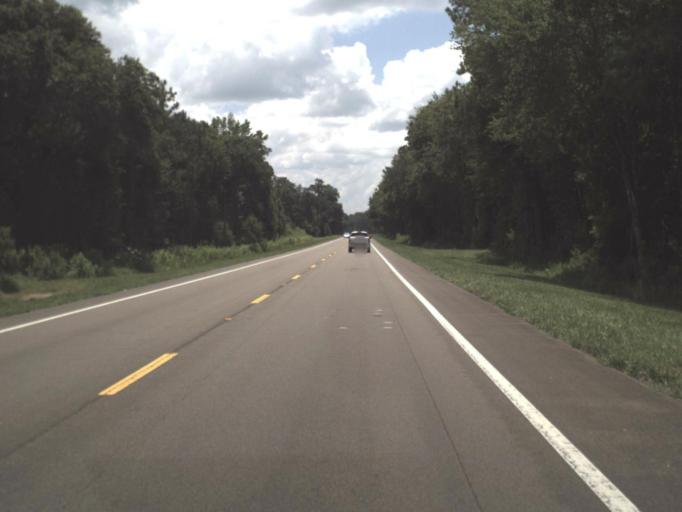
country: US
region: Florida
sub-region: Alachua County
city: Alachua
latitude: 29.7801
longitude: -82.3740
